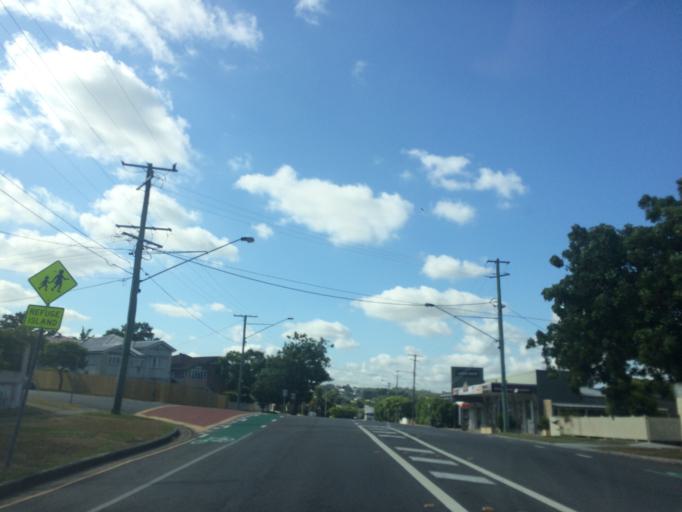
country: AU
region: Queensland
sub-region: Brisbane
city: Seven Hills
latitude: -27.4873
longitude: 153.0637
